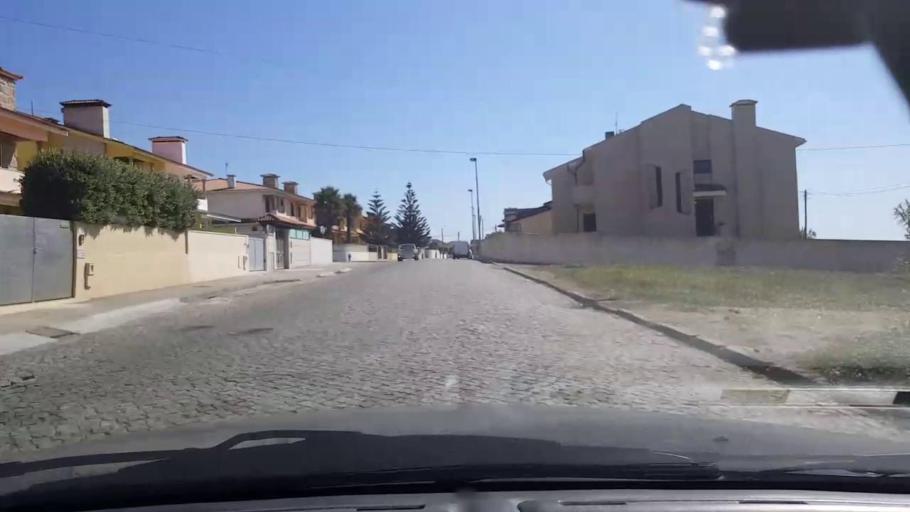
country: PT
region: Porto
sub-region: Vila do Conde
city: Arvore
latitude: 41.3025
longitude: -8.7356
